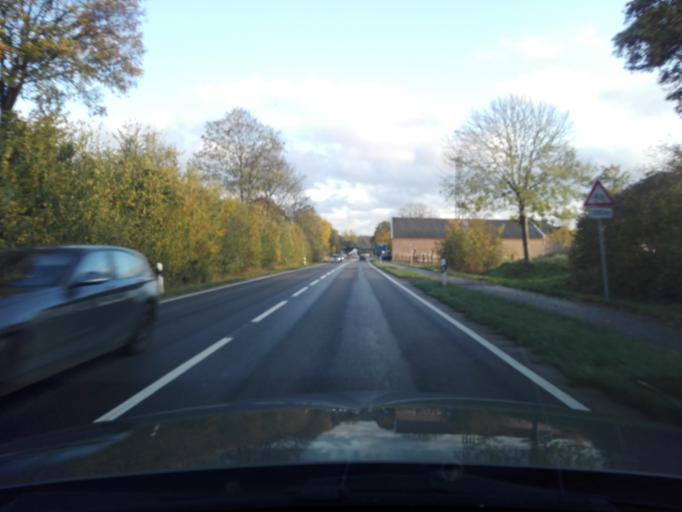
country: DE
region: North Rhine-Westphalia
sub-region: Regierungsbezirk Dusseldorf
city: Rheurdt
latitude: 51.4161
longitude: 6.4726
